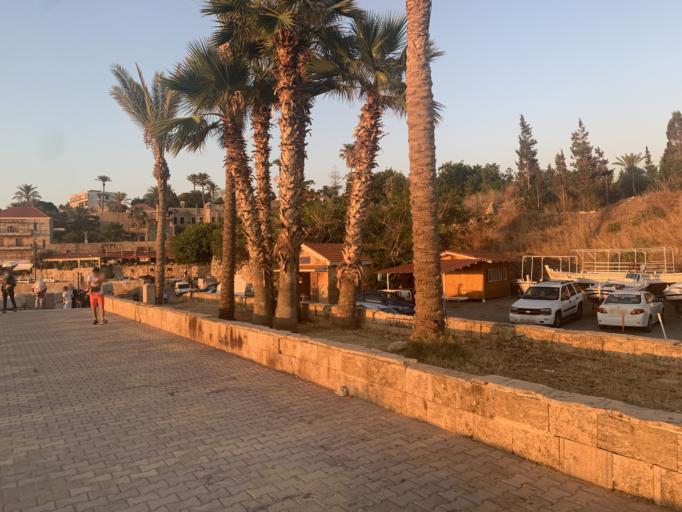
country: LB
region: Mont-Liban
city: Jbail
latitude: 34.1206
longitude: 35.6434
